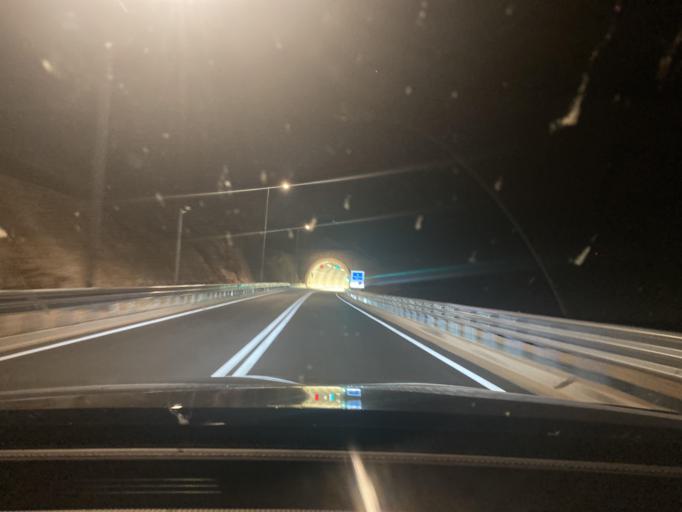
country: BA
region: Federation of Bosnia and Herzegovina
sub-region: Hercegovacko-Bosanski Kanton
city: Neum
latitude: 42.9037
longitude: 17.5440
